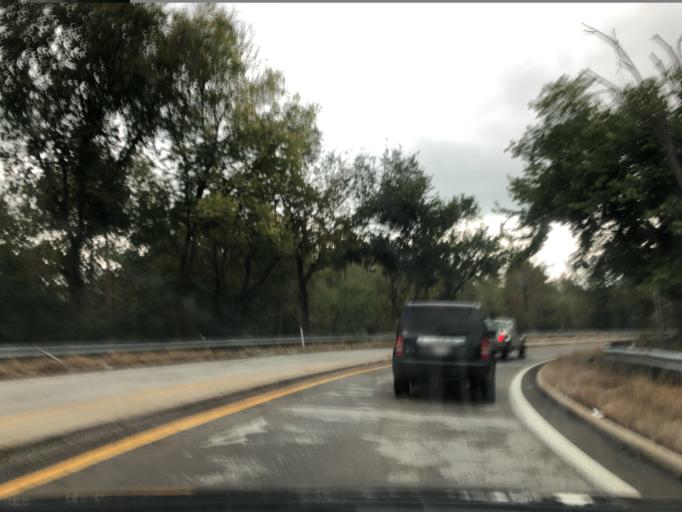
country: US
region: Ohio
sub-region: Hamilton County
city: Turpin Hills
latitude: 39.1065
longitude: -84.4001
